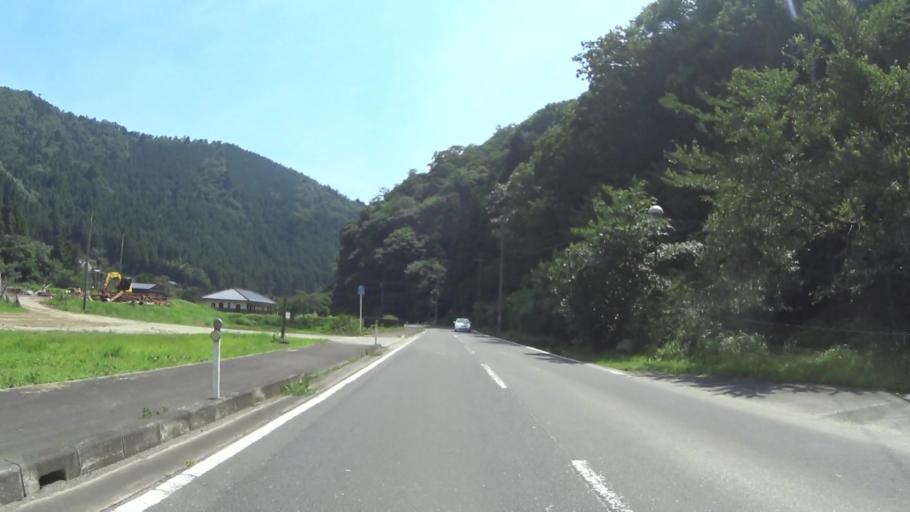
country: JP
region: Fukui
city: Obama
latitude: 35.3169
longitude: 135.5574
